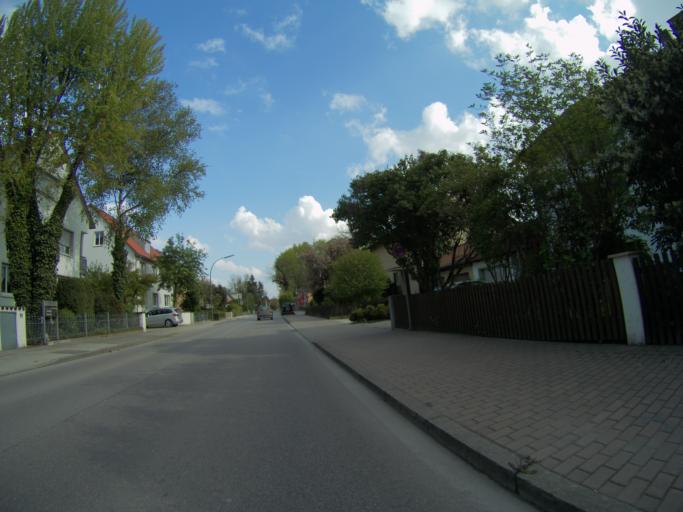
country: DE
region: Bavaria
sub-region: Upper Bavaria
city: Freising
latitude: 48.3900
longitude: 11.7638
